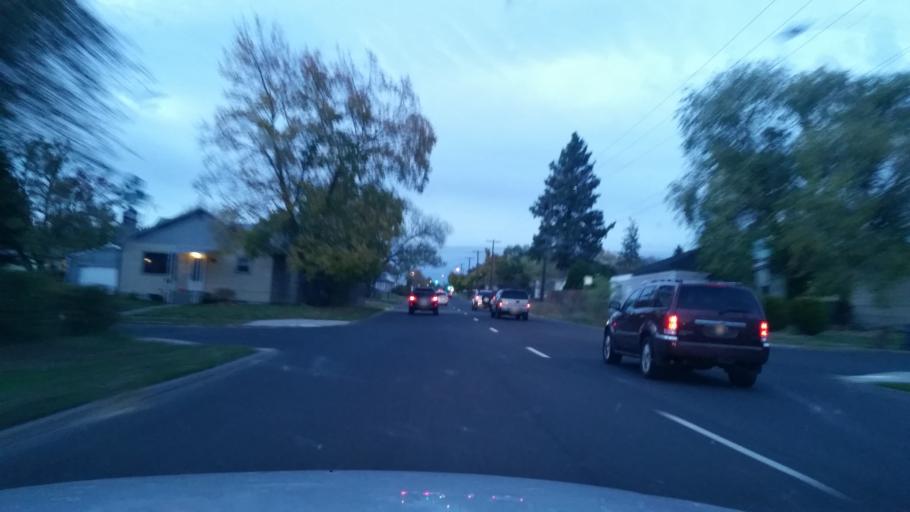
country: US
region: Washington
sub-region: Spokane County
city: Spokane
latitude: 47.6900
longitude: -117.4351
